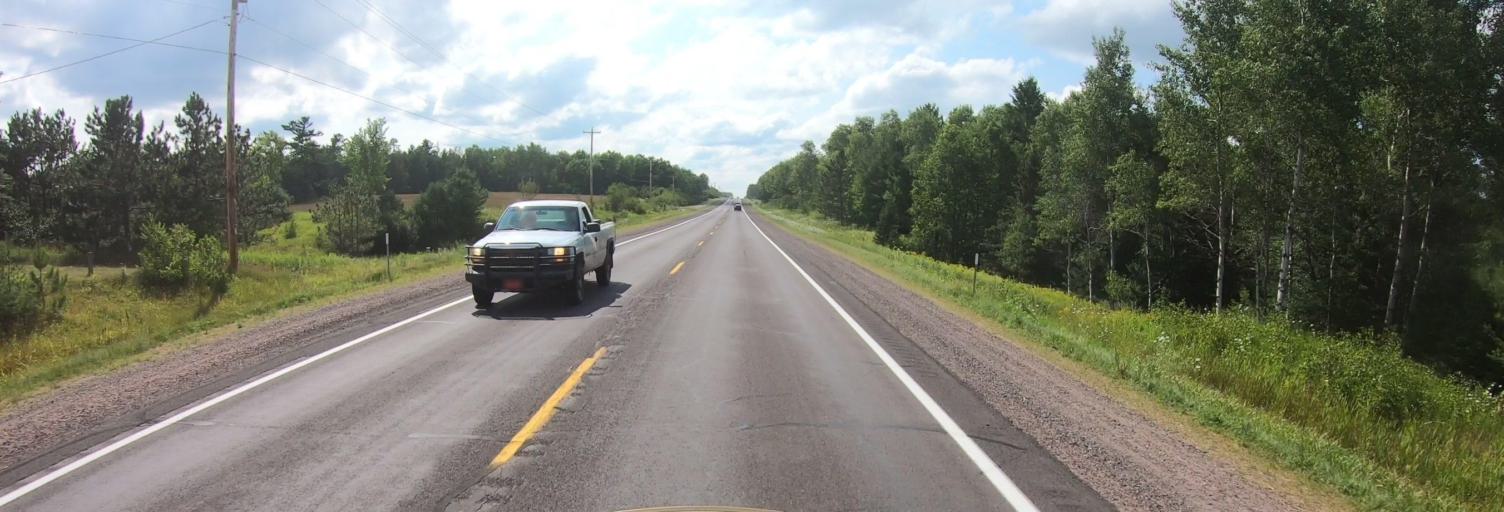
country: US
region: Michigan
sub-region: Ontonagon County
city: Ontonagon
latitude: 46.5348
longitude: -89.2224
